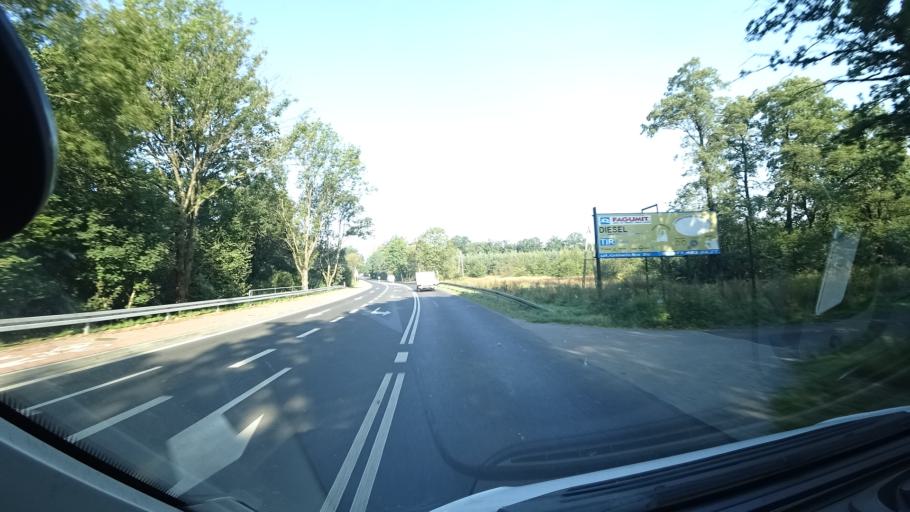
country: PL
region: Opole Voivodeship
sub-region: Powiat kedzierzynsko-kozielski
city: Kedzierzyn-Kozle
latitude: 50.3201
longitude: 18.2216
